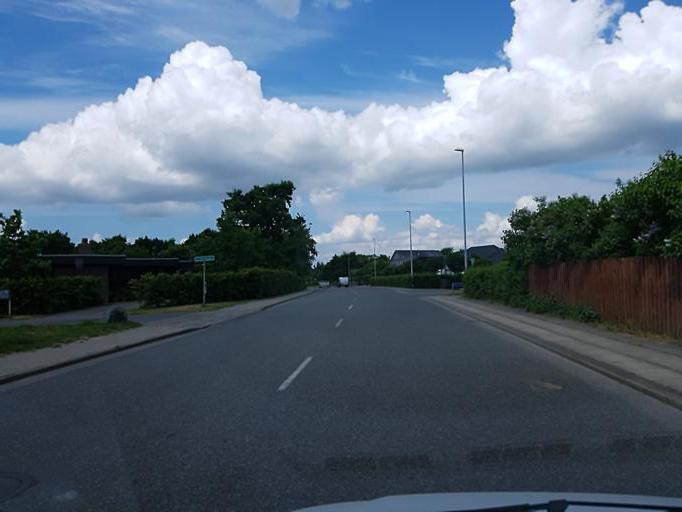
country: DK
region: South Denmark
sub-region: Fano Kommune
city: Nordby
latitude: 55.5327
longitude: 8.3481
